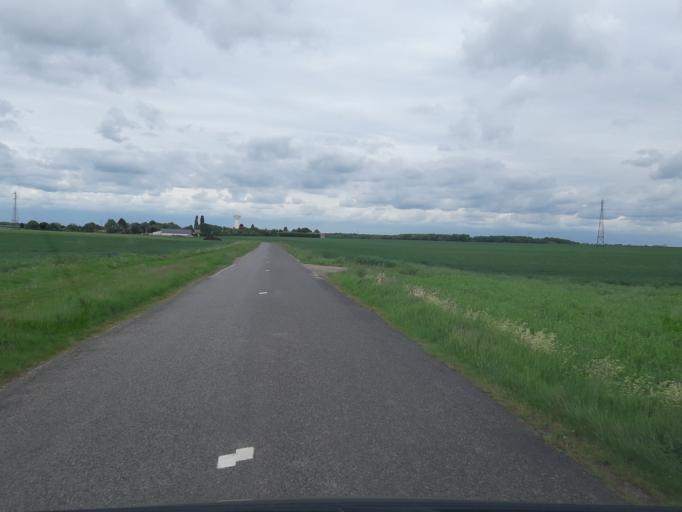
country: FR
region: Ile-de-France
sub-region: Departement de l'Essonne
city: Saclas
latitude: 48.3685
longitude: 2.1874
